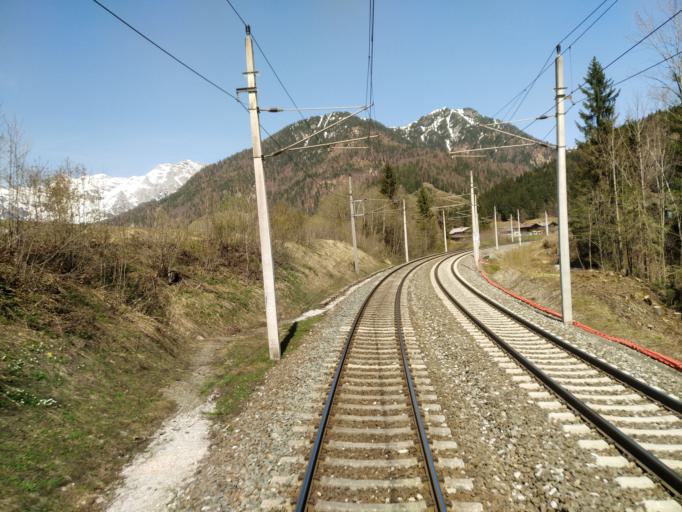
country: AT
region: Tyrol
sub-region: Politischer Bezirk Kitzbuhel
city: Hochfilzen
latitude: 47.4734
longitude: 12.6107
